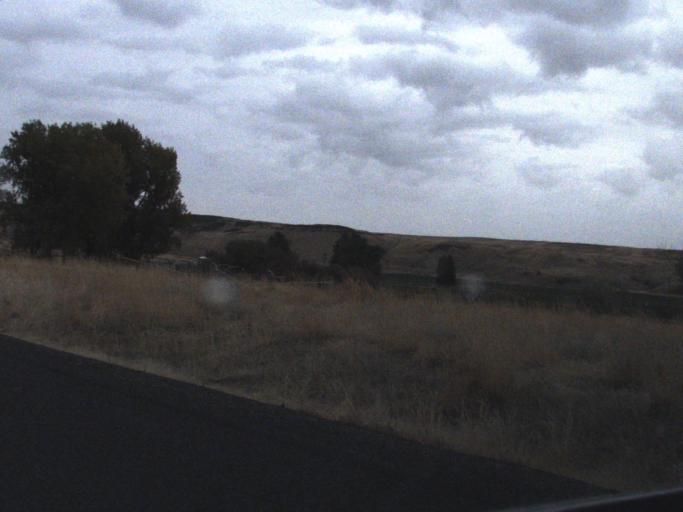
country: US
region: Washington
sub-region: Adams County
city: Ritzville
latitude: 46.7444
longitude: -118.2067
